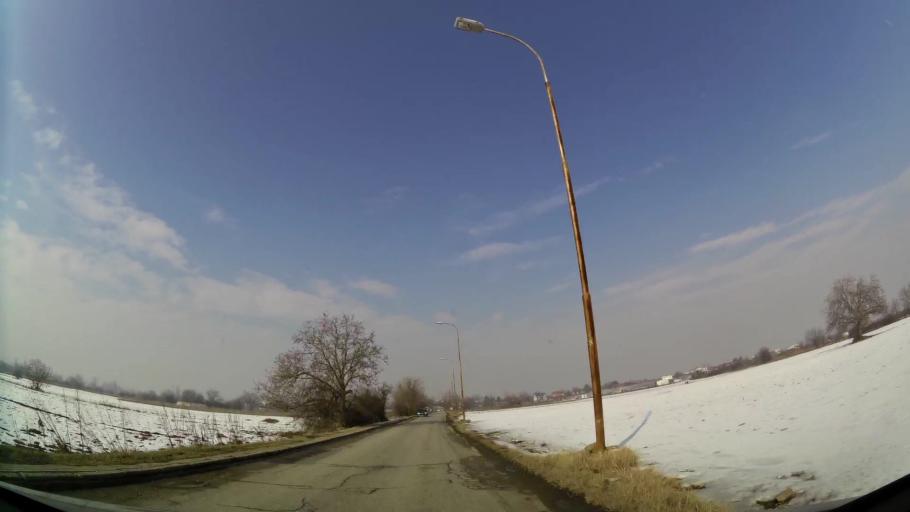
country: MK
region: Suto Orizari
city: Suto Orizare
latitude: 42.0210
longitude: 21.3871
